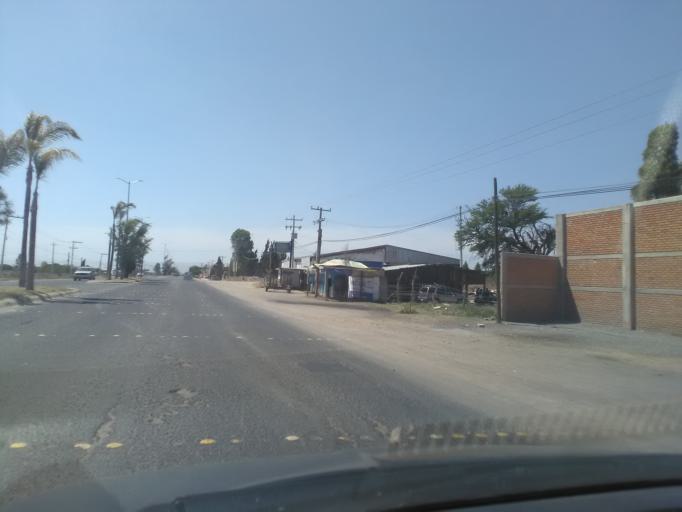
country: MX
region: Durango
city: Victoria de Durango
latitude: 24.0271
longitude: -104.5808
